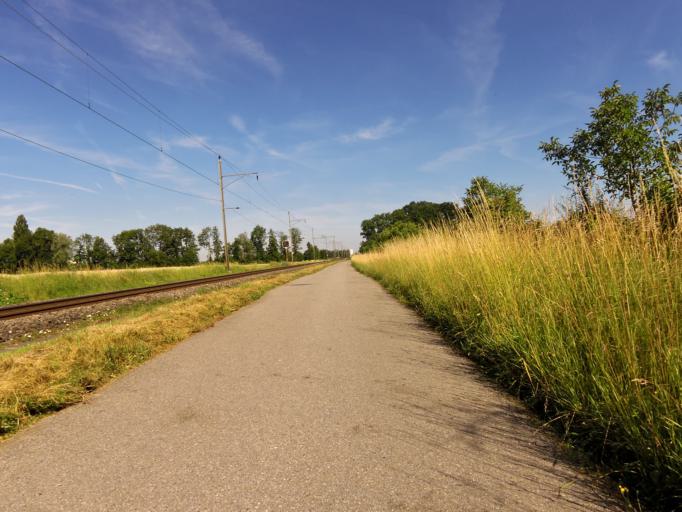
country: CH
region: Thurgau
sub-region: Kreuzlingen District
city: Guttingen
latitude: 47.6016
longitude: 9.3056
